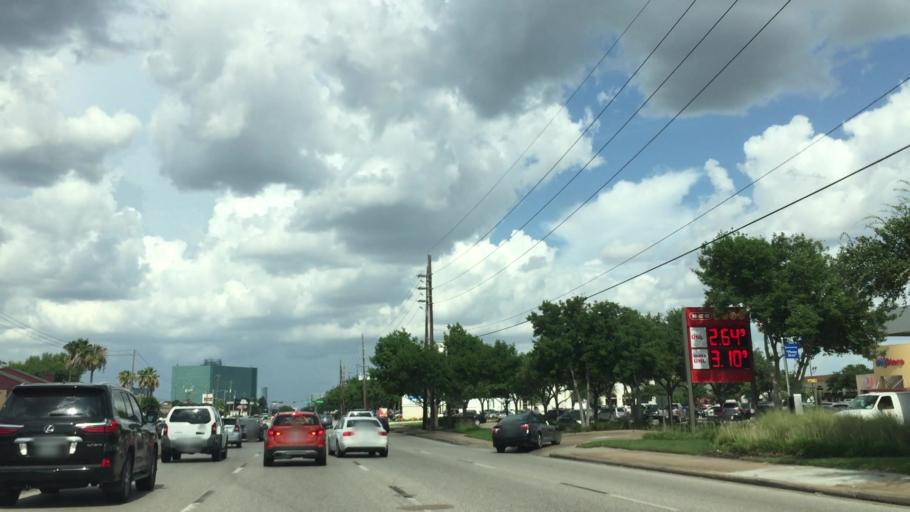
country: US
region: Texas
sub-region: Harris County
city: Bunker Hill Village
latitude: 29.7364
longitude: -95.5884
